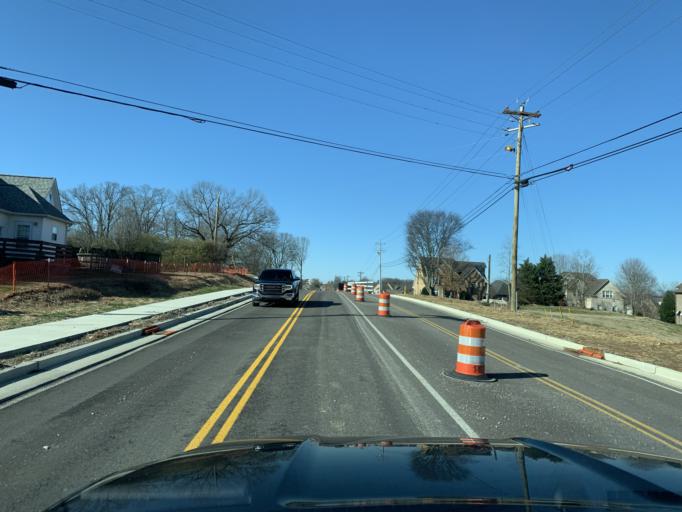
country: US
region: Tennessee
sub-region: Maury County
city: Spring Hill
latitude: 35.7527
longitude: -86.8875
